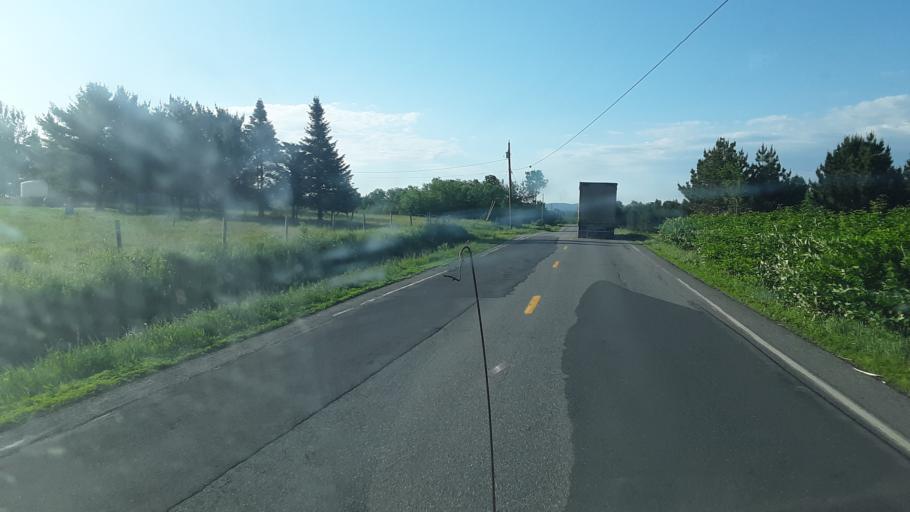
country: US
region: Maine
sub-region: Penobscot County
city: Patten
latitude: 46.1554
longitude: -68.2210
